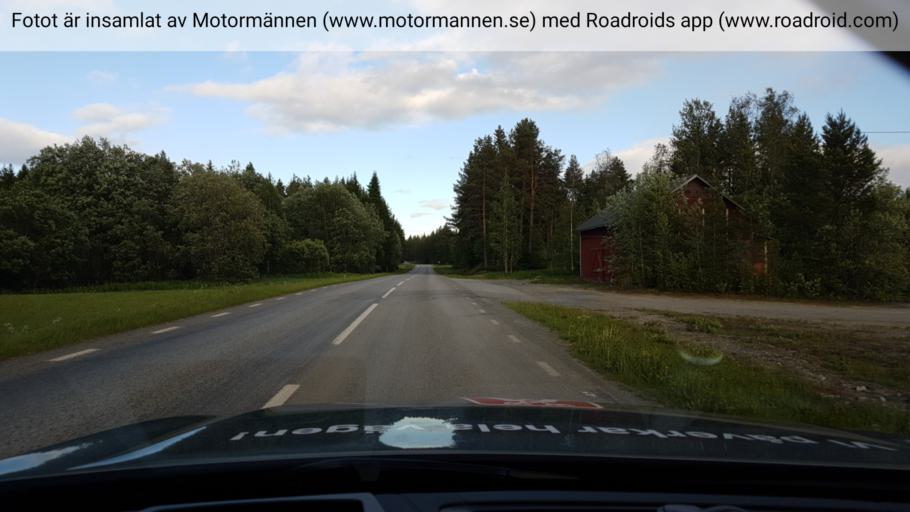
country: SE
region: Jaemtland
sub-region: Krokoms Kommun
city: Krokom
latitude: 63.1376
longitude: 14.1936
